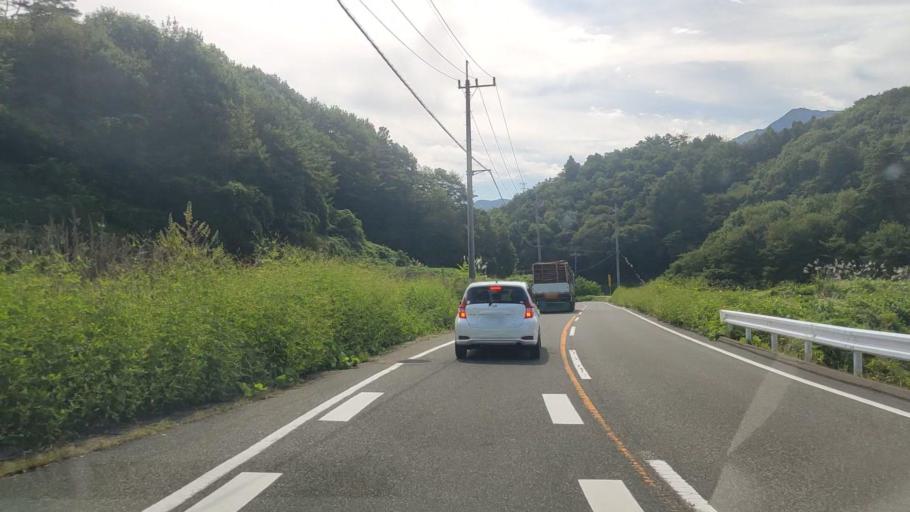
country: JP
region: Gunma
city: Numata
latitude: 36.6303
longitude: 138.9968
